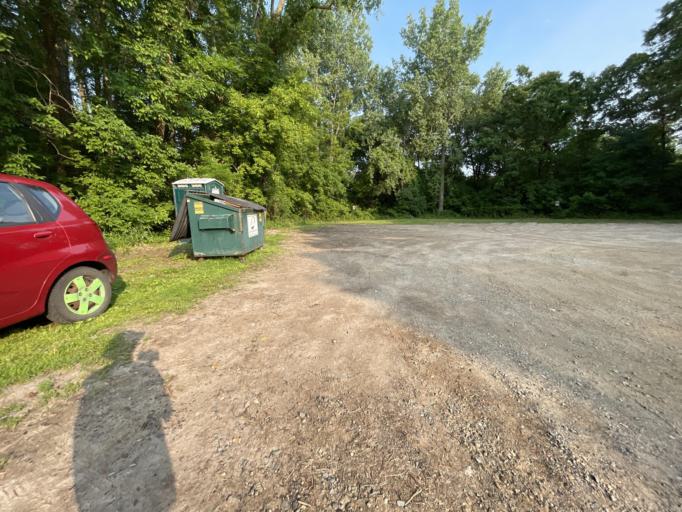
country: US
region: Minnesota
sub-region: Sherburne County
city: Becker
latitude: 45.5066
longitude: -93.9266
